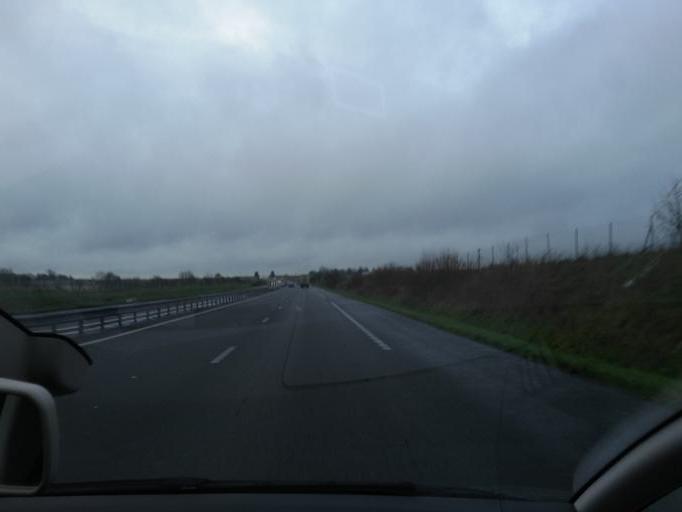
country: FR
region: Nord-Pas-de-Calais
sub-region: Departement du Pas-de-Calais
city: Hermies
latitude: 50.0690
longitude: 2.9920
